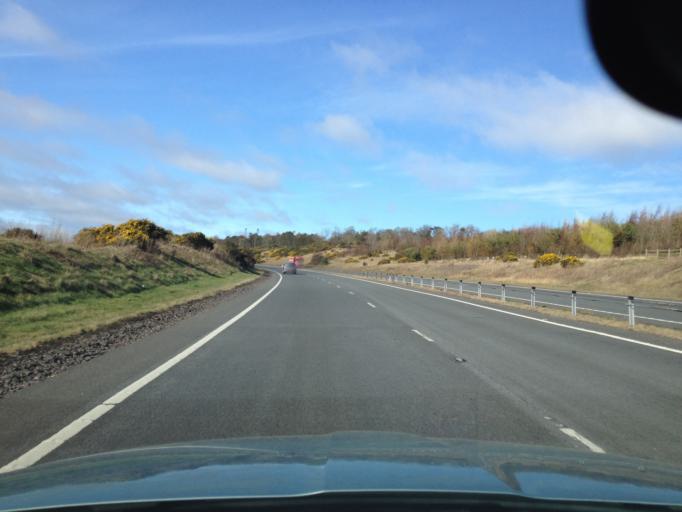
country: GB
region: Scotland
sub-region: East Lothian
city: East Linton
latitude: 55.9792
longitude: -2.6788
